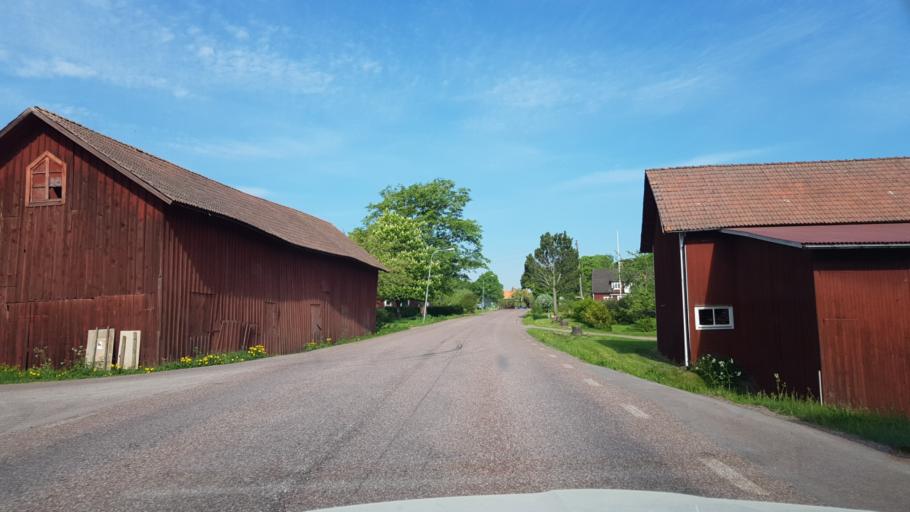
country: SE
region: Dalarna
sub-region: Saters Kommun
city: Saeter
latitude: 60.4221
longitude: 15.6600
